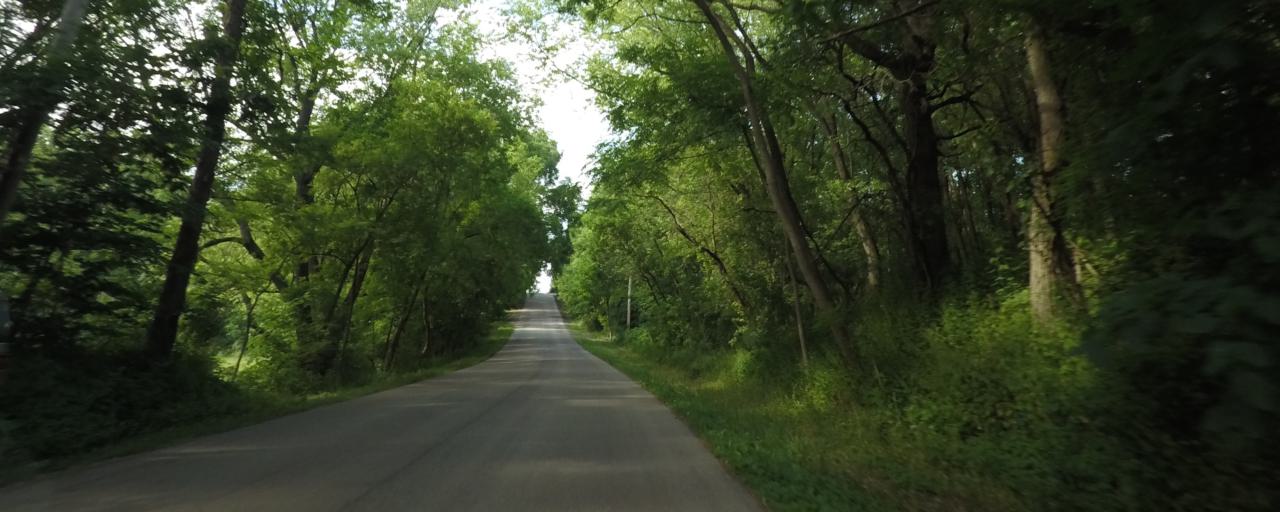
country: US
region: Wisconsin
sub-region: Walworth County
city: Elkhorn
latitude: 42.7699
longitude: -88.5439
